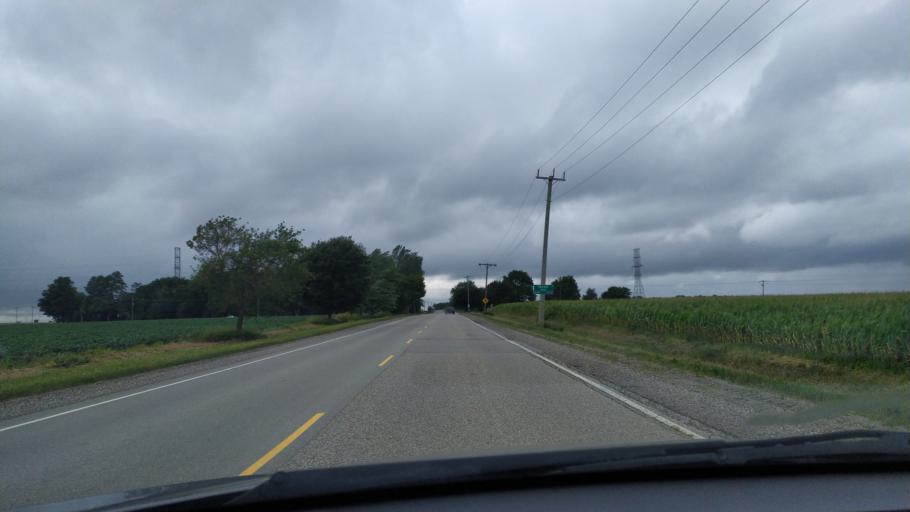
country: CA
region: Ontario
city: Kitchener
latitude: 43.3489
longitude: -80.6938
